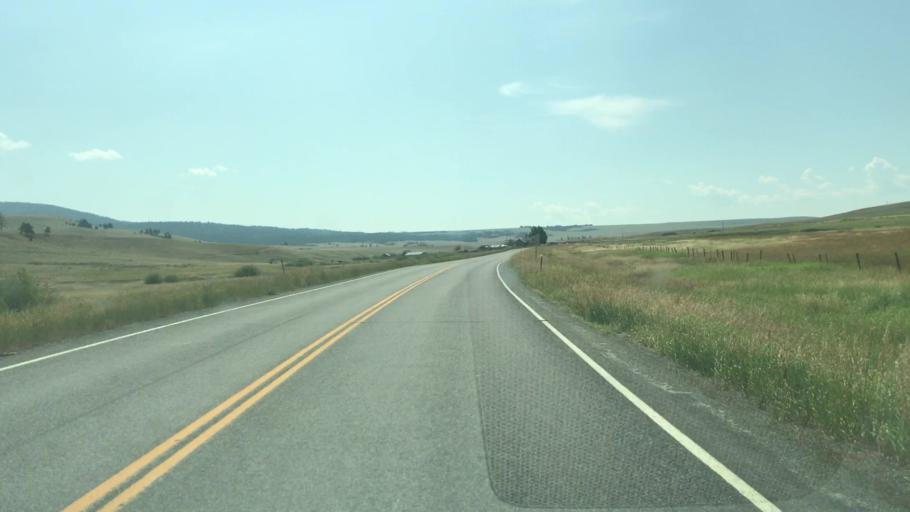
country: US
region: Montana
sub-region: Lewis and Clark County
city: Lincoln
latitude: 46.7424
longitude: -112.6841
